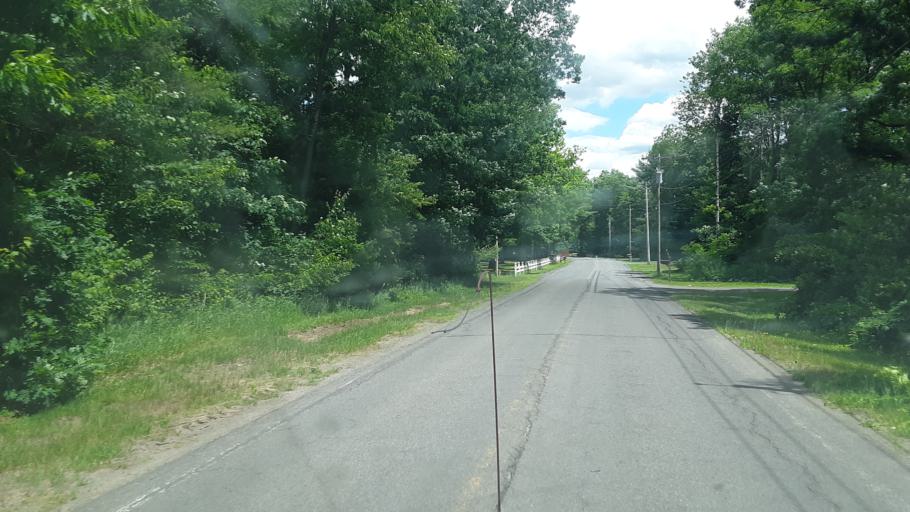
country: US
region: New York
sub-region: Oneida County
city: Rome
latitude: 43.2634
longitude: -75.5665
